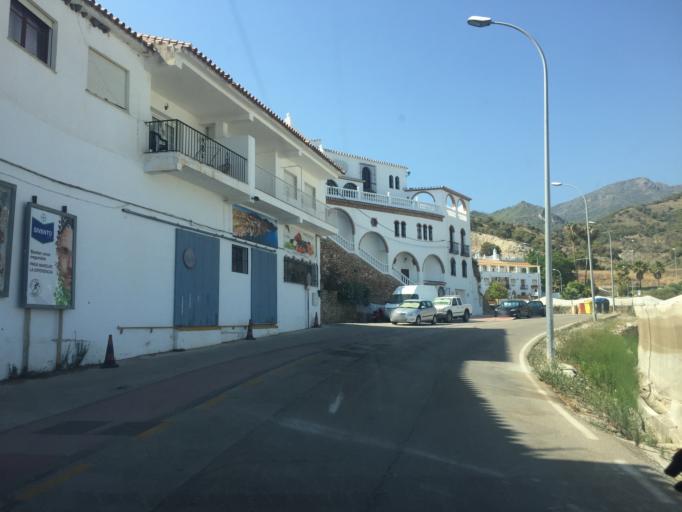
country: ES
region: Andalusia
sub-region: Provincia de Malaga
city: Nerja
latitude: 36.7579
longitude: -3.8422
